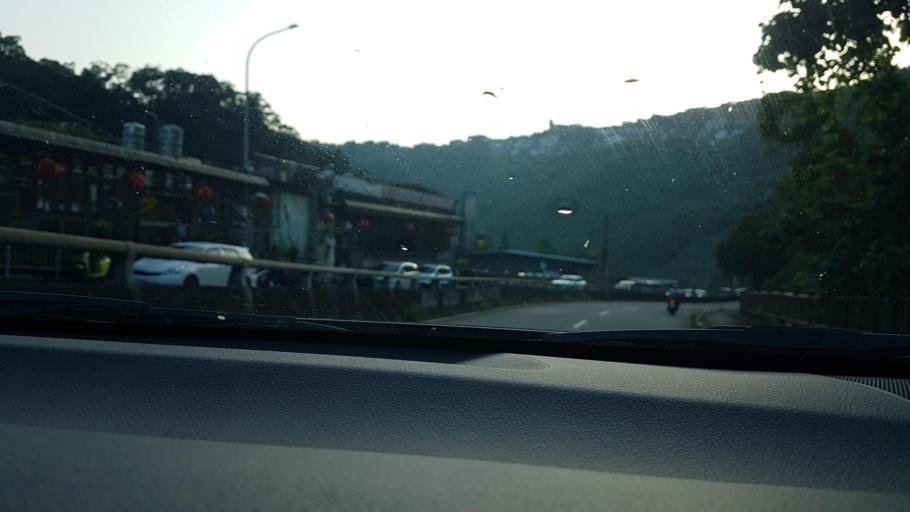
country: TW
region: Taipei
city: Taipei
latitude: 25.1123
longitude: 121.5622
